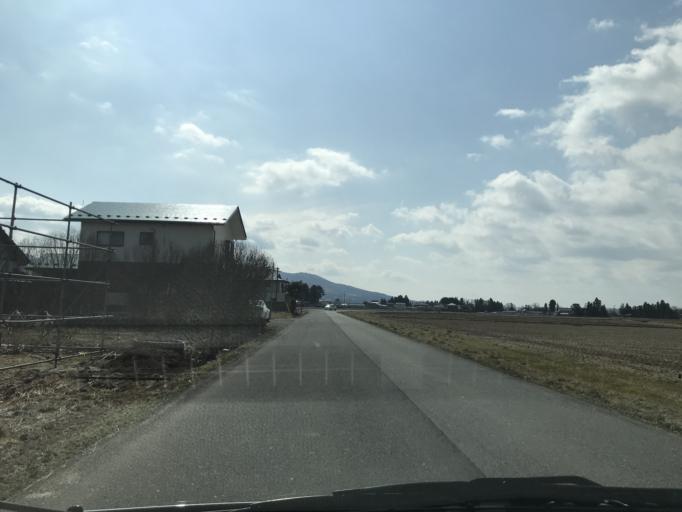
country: JP
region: Iwate
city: Mizusawa
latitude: 39.0707
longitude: 141.1417
